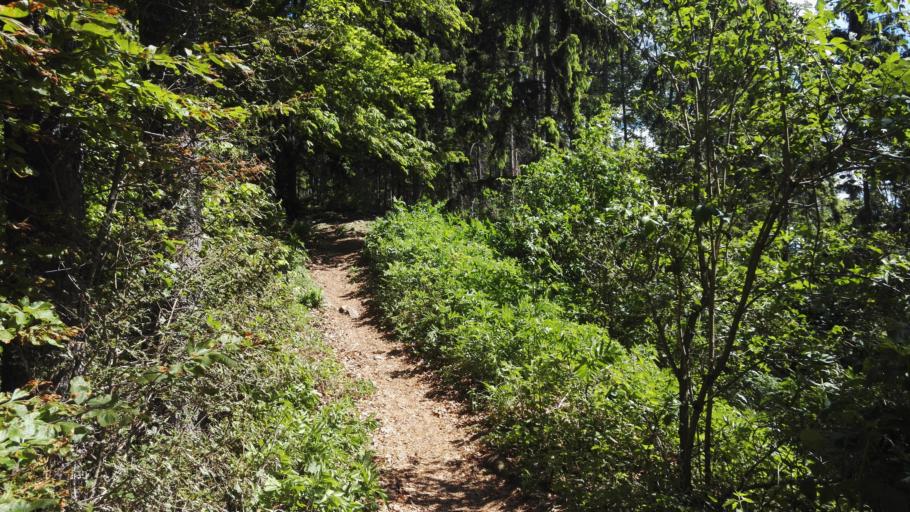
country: AT
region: Styria
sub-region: Graz Stadt
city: Goesting
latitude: 47.0870
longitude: 15.3839
